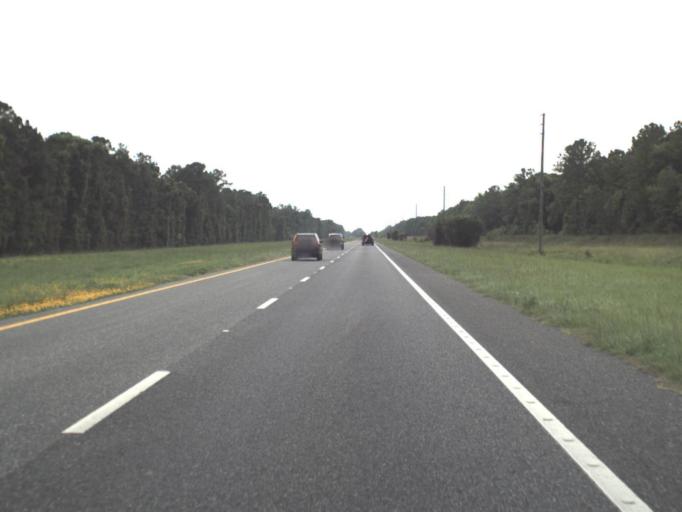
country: US
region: Florida
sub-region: Levy County
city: Williston Highlands
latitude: 29.2285
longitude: -82.7080
